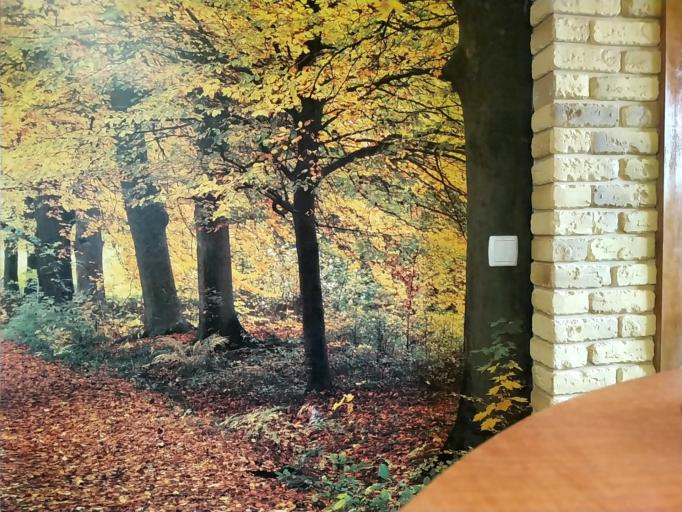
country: RU
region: Novgorod
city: Opechenskiy Posad
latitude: 58.2706
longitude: 34.0088
